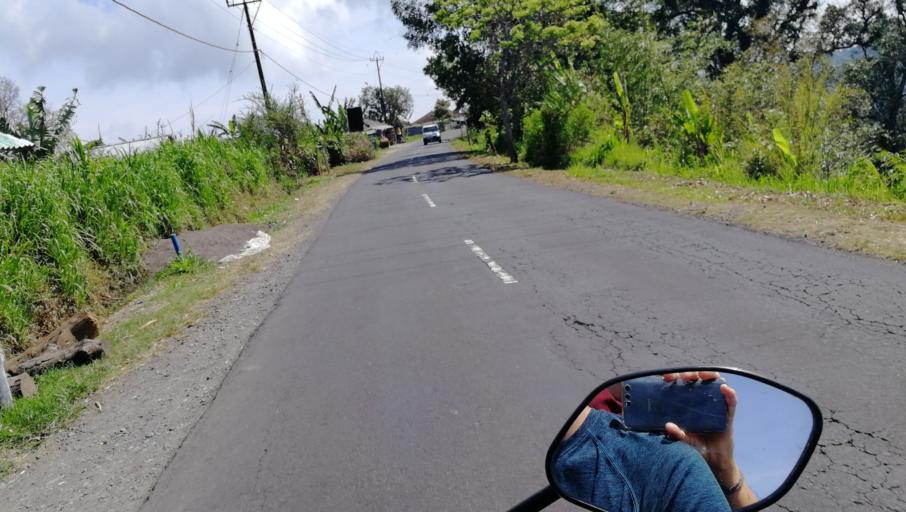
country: ID
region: Bali
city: Munduk
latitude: -8.2454
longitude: 115.1012
